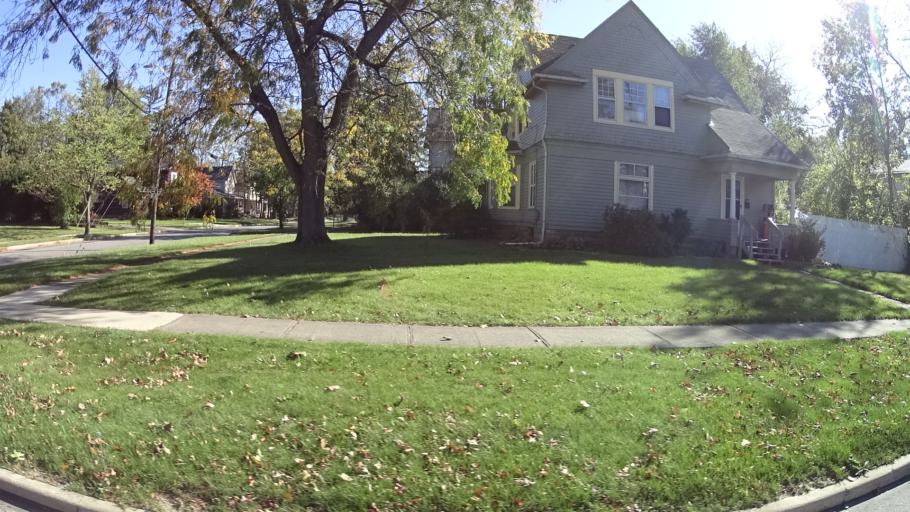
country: US
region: Ohio
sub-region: Lorain County
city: Oberlin
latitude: 41.2861
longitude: -82.2176
